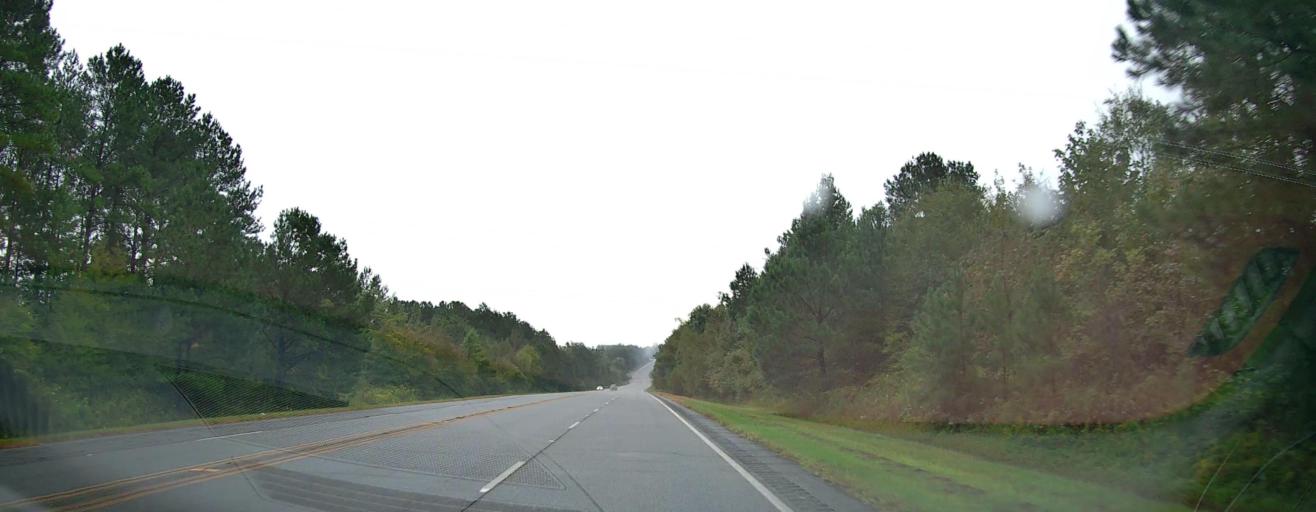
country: US
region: Georgia
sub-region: Bleckley County
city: Cochran
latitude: 32.5152
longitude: -83.4275
